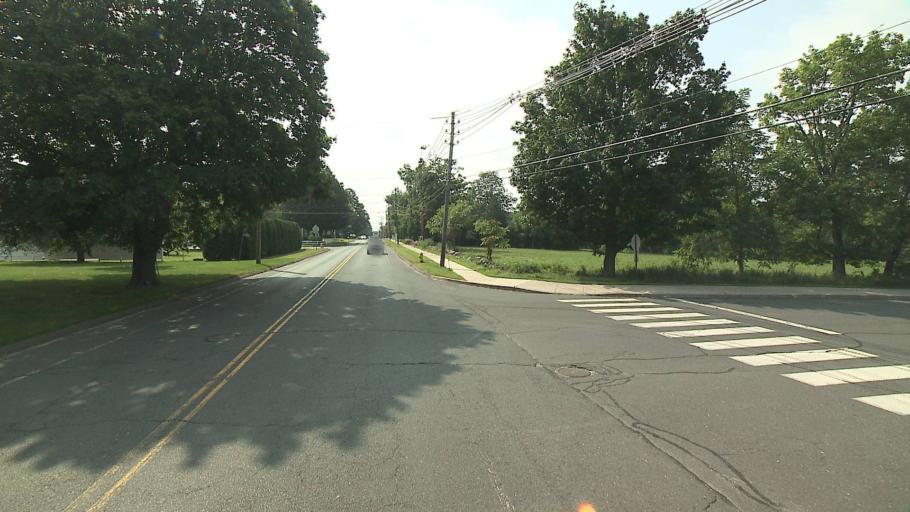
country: US
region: Connecticut
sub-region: Litchfield County
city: Oakville
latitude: 41.6067
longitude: -73.0904
